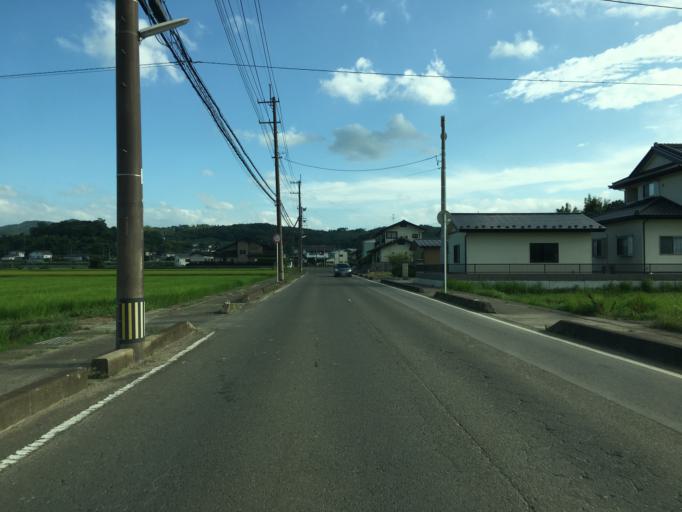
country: JP
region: Fukushima
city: Hobaramachi
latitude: 37.8076
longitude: 140.5515
